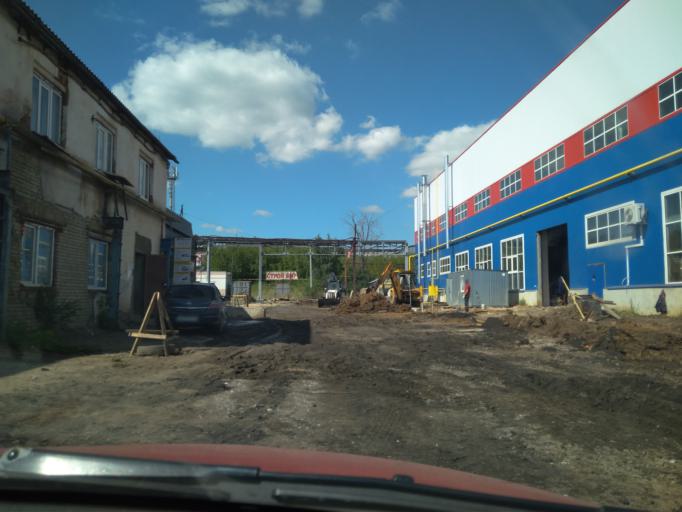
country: RU
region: Mordoviya
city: Saransk
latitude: 54.2062
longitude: 45.1784
